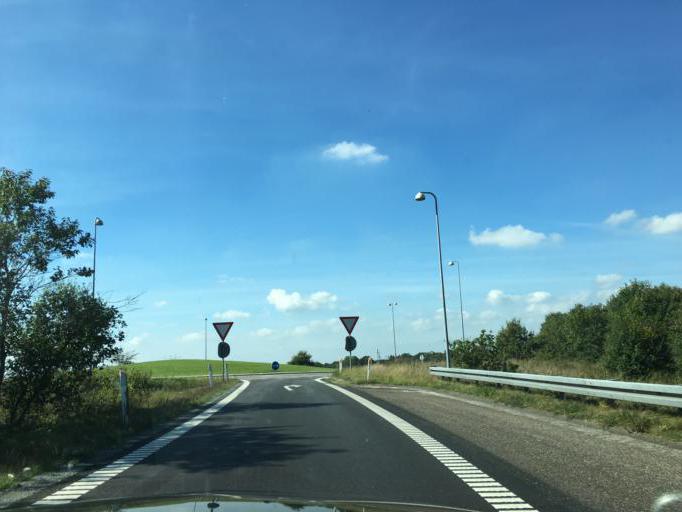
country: DK
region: South Denmark
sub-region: Kolding Kommune
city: Lunderskov
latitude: 55.5048
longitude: 9.2773
